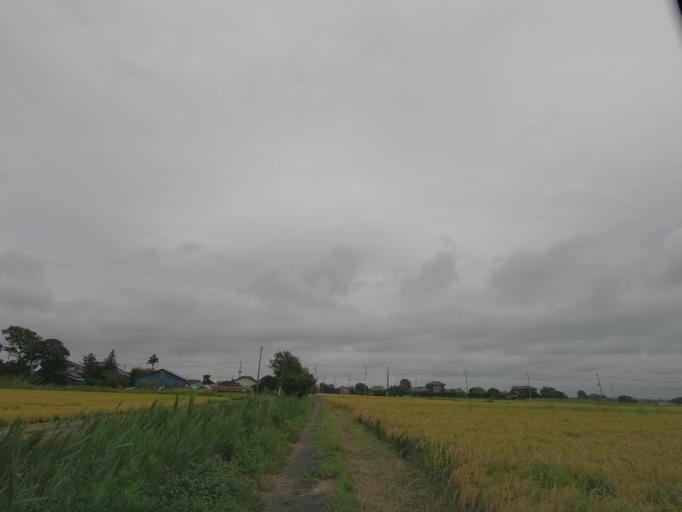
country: JP
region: Ibaraki
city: Toride
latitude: 35.9248
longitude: 140.0707
